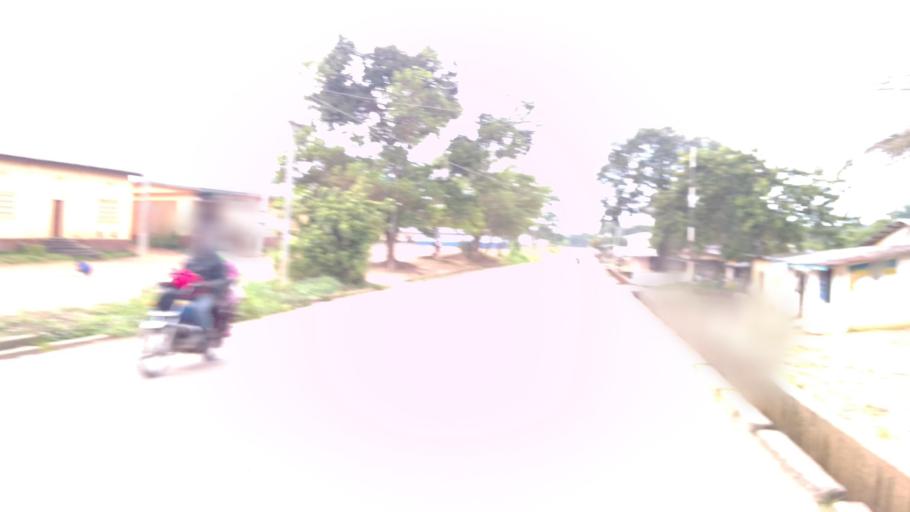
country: SL
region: Eastern Province
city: Koidu
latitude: 8.6538
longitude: -10.9755
